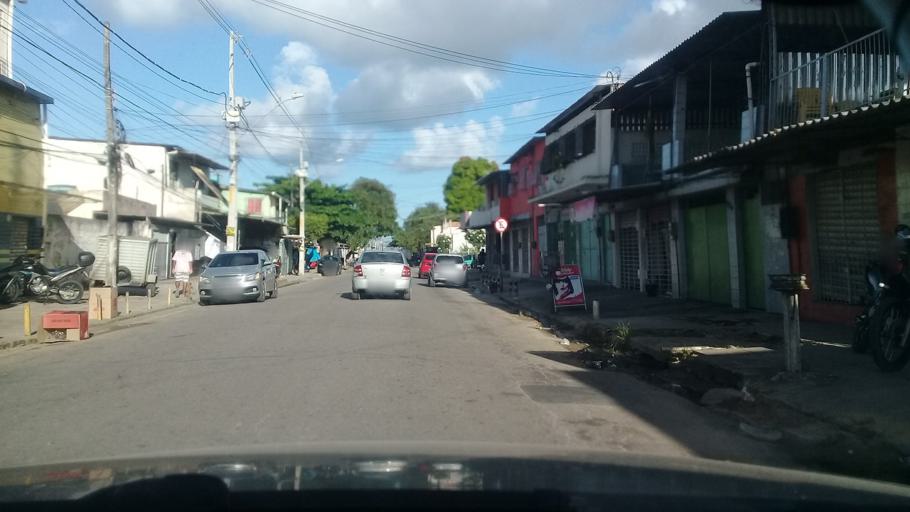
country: BR
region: Pernambuco
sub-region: Jaboatao Dos Guararapes
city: Jaboatao dos Guararapes
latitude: -8.1189
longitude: -34.9403
